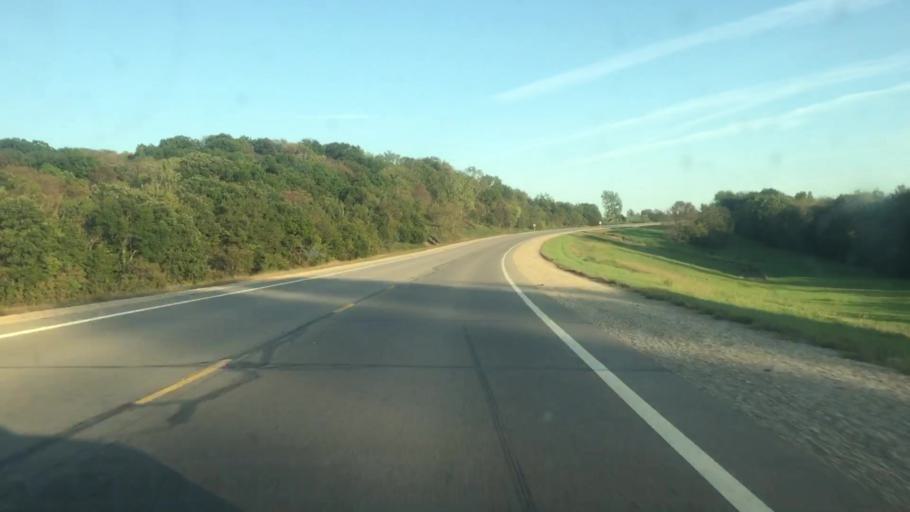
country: US
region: Kansas
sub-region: Atchison County
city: Atchison
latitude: 39.4836
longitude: -95.1132
